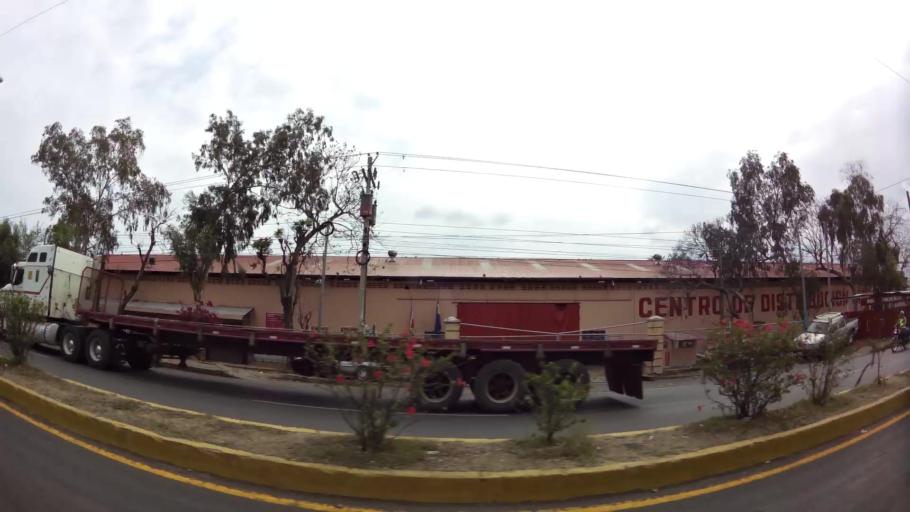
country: NI
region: Masaya
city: Masaya
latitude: 11.9873
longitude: -86.0951
